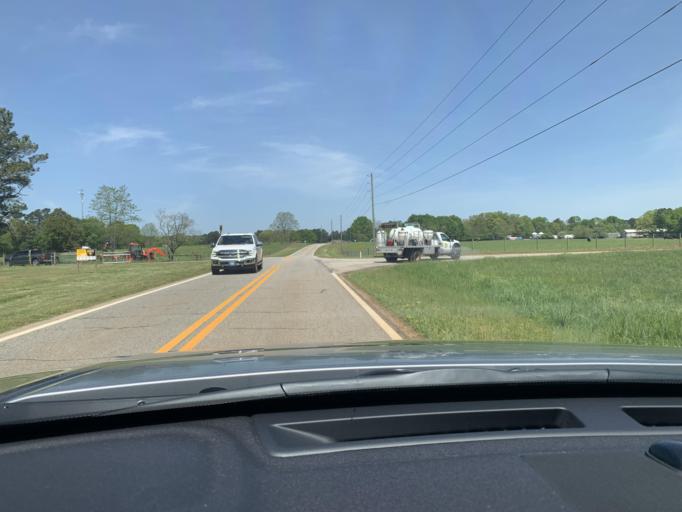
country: US
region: Georgia
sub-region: Oconee County
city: Bogart
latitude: 33.9272
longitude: -83.5615
